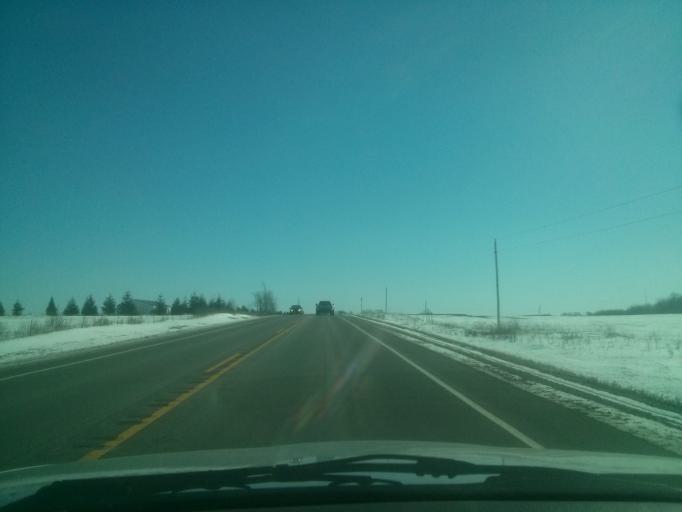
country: US
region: Wisconsin
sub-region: Polk County
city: Clear Lake
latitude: 45.1363
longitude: -92.3087
